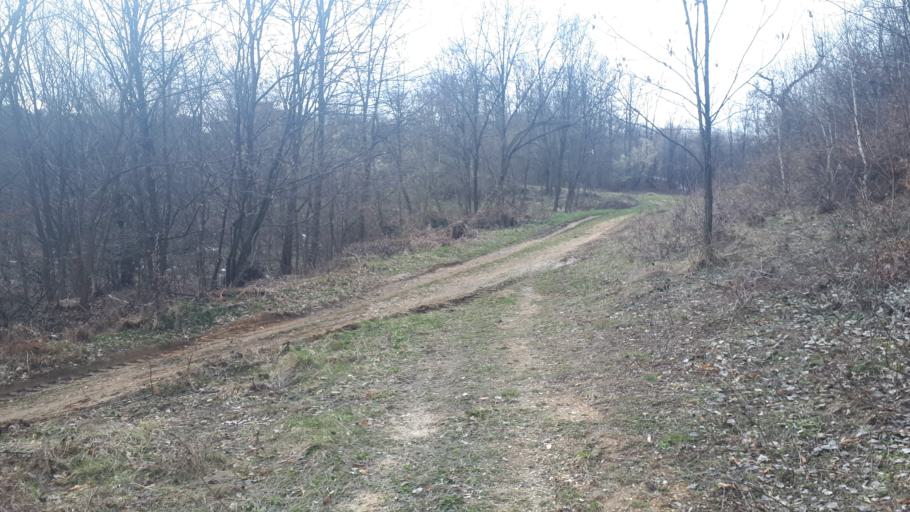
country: RS
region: Central Serbia
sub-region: Zlatiborski Okrug
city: Uzice
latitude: 43.8482
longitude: 19.8784
